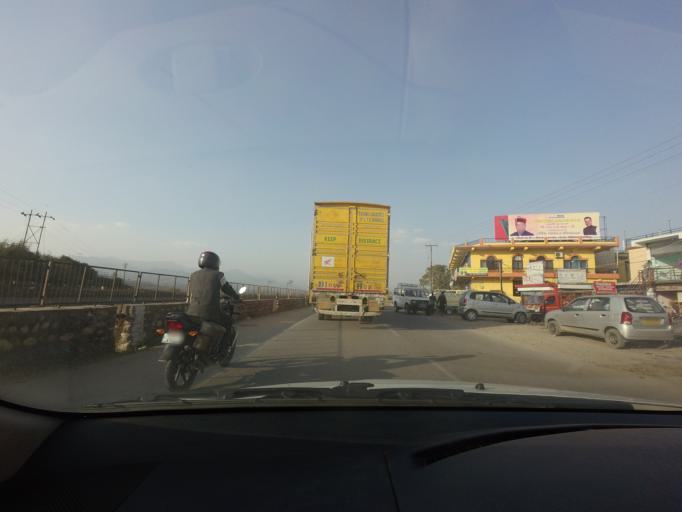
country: IN
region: Himachal Pradesh
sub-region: Mandi
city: Sundarnagar
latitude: 31.5428
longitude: 76.8972
